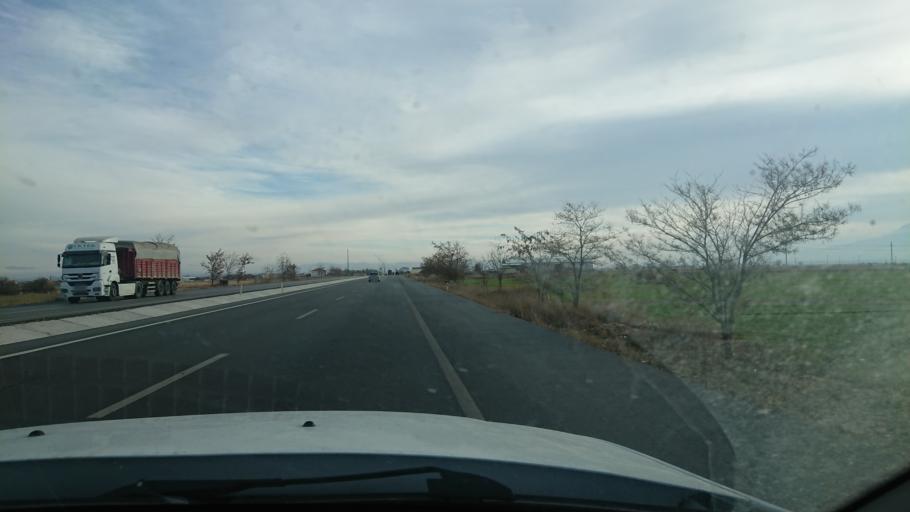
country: TR
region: Aksaray
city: Yesilova
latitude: 38.2886
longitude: 33.7493
